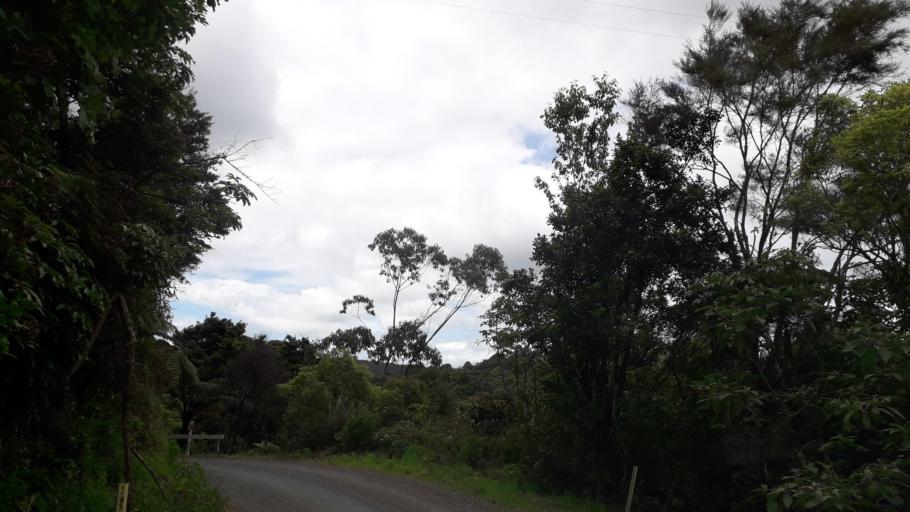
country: NZ
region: Northland
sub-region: Far North District
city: Taipa
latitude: -35.0889
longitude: 173.5508
